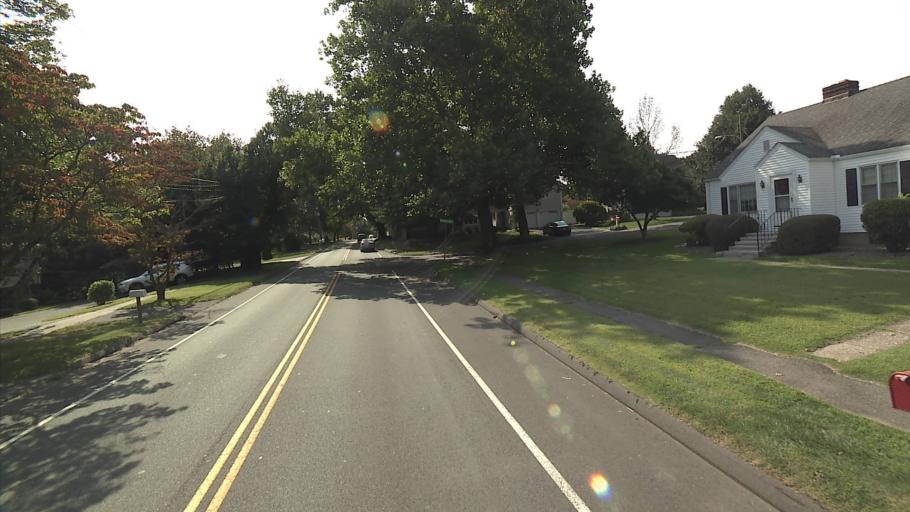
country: US
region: Connecticut
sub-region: Fairfield County
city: Fairfield
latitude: 41.1697
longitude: -73.2584
